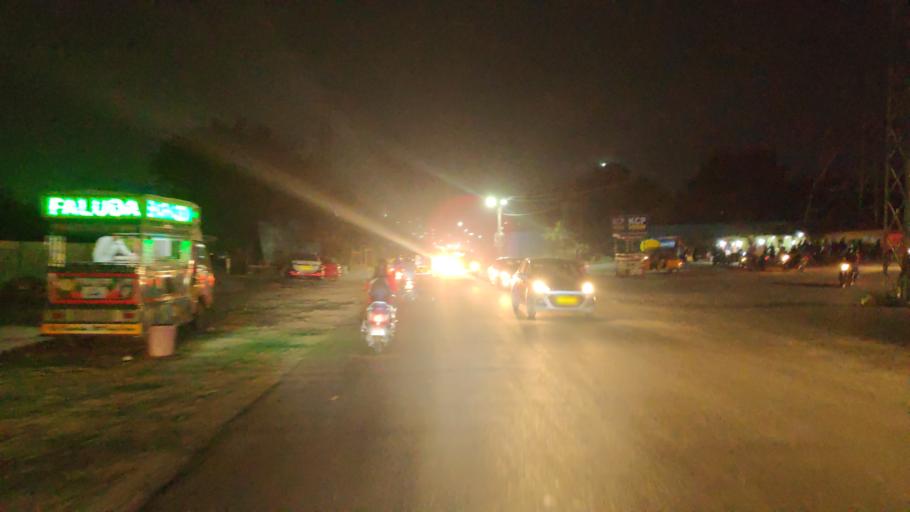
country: IN
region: Telangana
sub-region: Rangareddi
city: Kukatpalli
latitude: 17.4773
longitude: 78.3786
